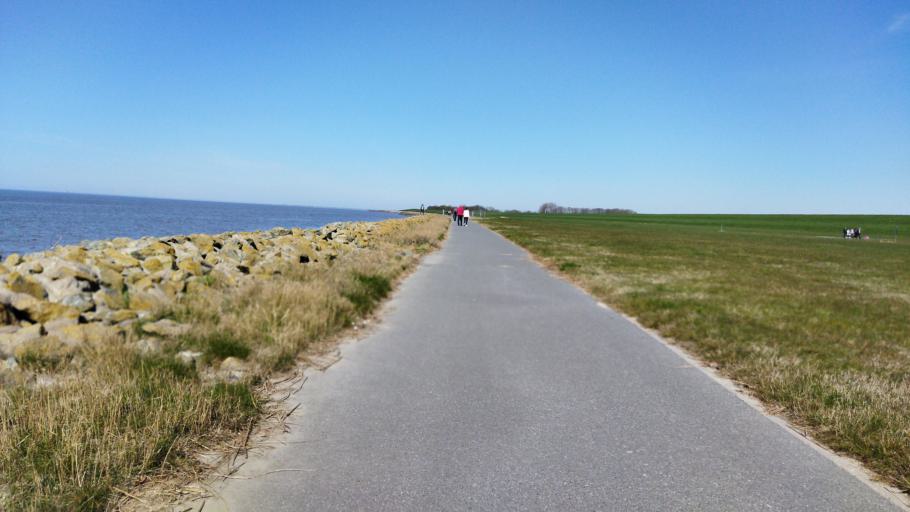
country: DE
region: Lower Saxony
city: Wremen
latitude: 53.6157
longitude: 8.5145
